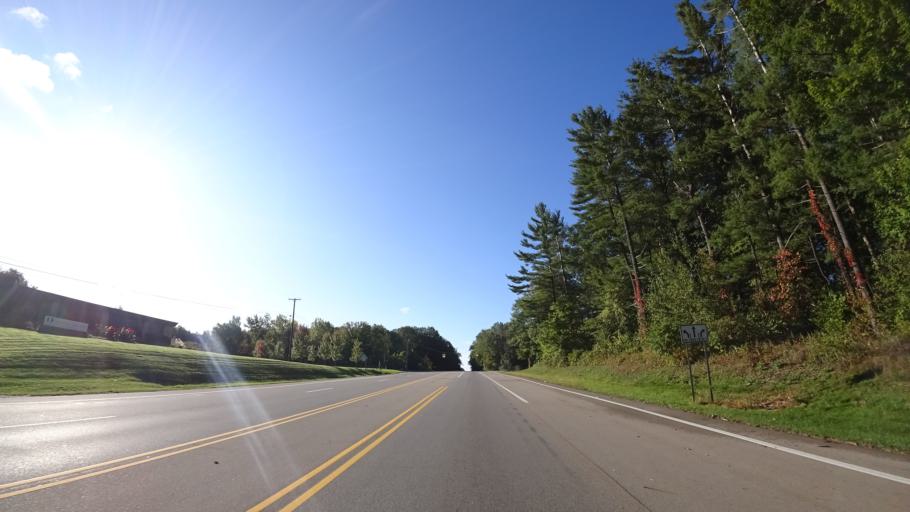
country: US
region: Michigan
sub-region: Kent County
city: Grandville
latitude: 42.9296
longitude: -85.7740
